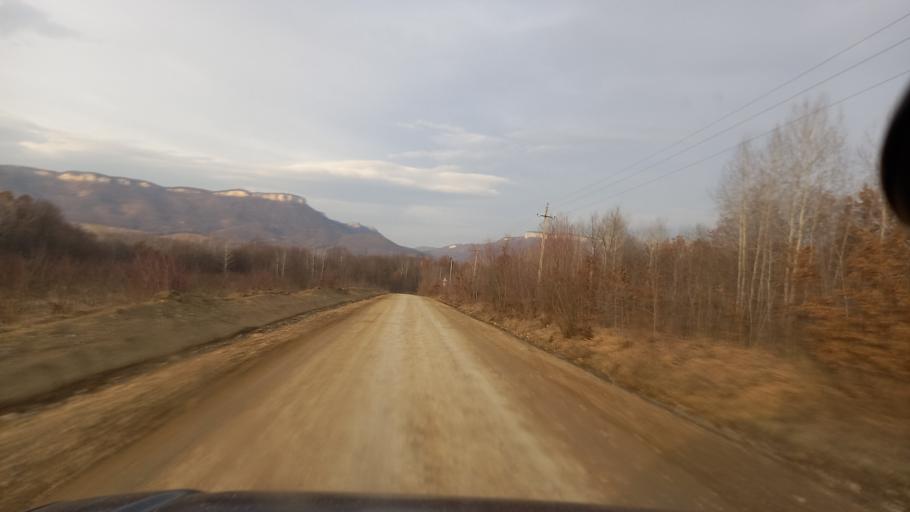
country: RU
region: Adygeya
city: Kamennomostskiy
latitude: 44.1861
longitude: 40.2608
